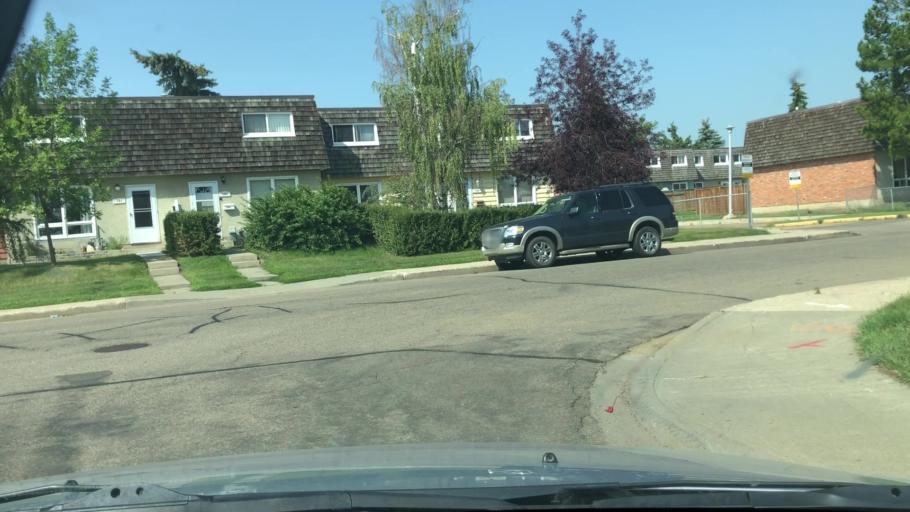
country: CA
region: Alberta
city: Edmonton
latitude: 53.6055
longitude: -113.4731
